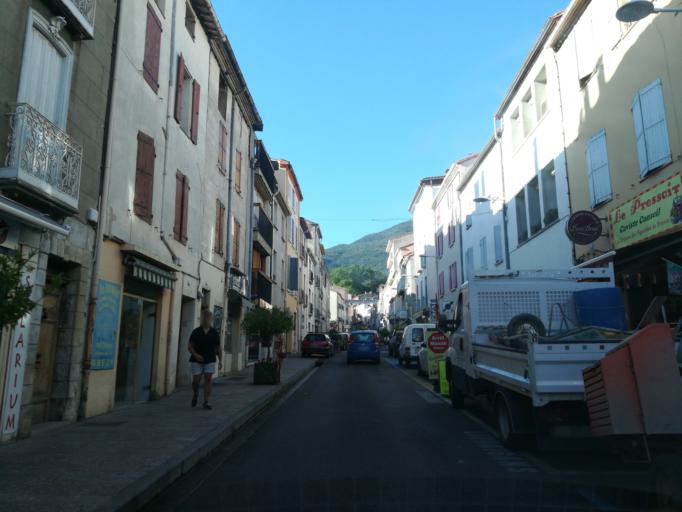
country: FR
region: Languedoc-Roussillon
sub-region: Departement des Pyrenees-Orientales
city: Ceret
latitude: 42.4881
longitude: 2.7476
